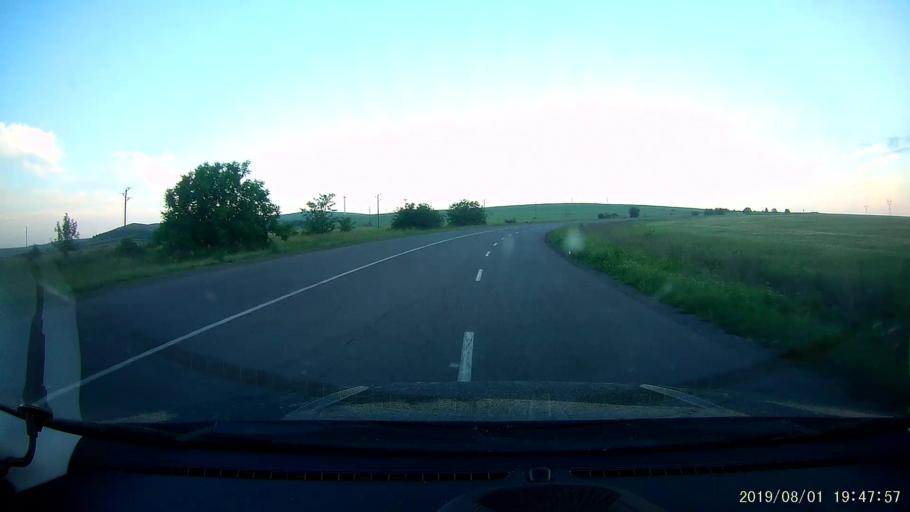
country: BG
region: Burgas
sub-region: Obshtina Karnobat
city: Karnobat
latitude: 42.6439
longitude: 26.9575
